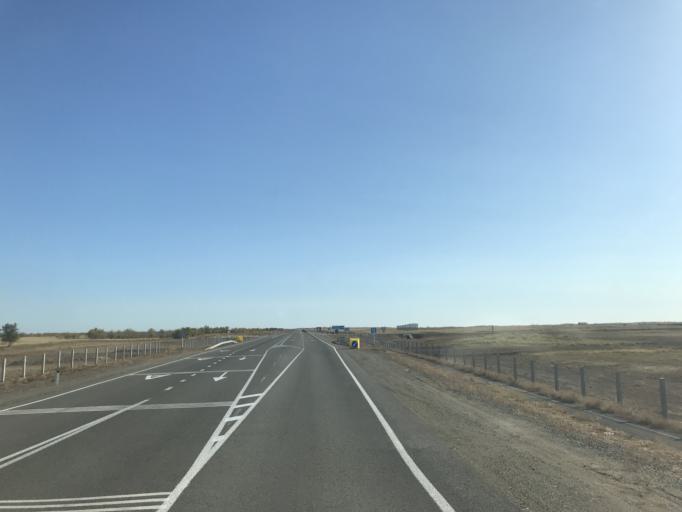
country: KZ
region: Pavlodar
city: Koktobe
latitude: 51.8160
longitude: 77.4698
